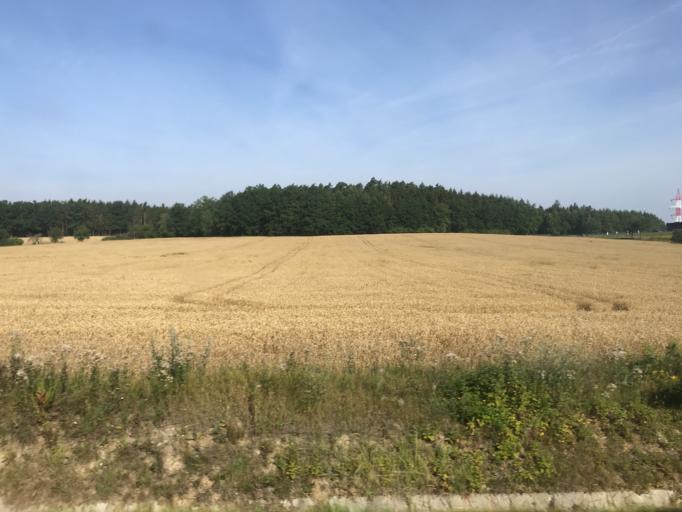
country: CZ
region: Jihocesky
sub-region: Okres Tabor
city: Tabor
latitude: 49.4362
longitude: 14.6880
